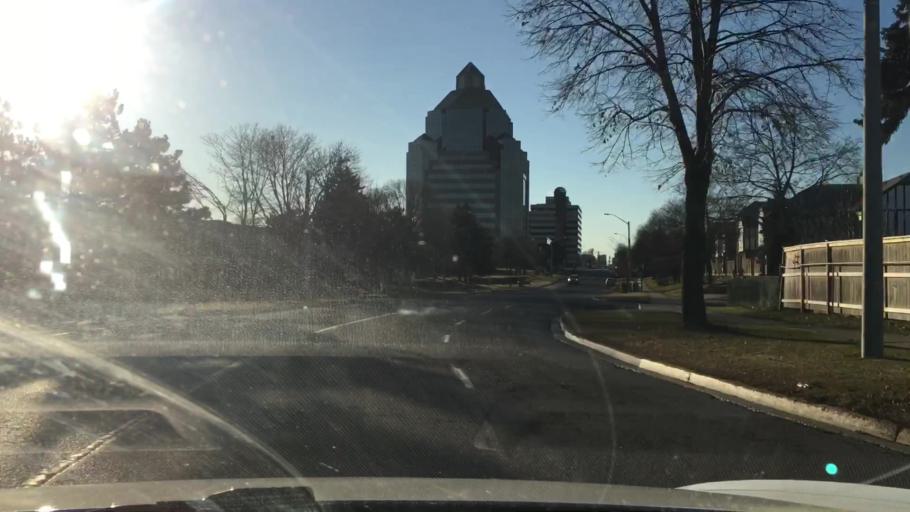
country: CA
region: Ontario
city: Scarborough
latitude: 43.7913
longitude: -79.2292
